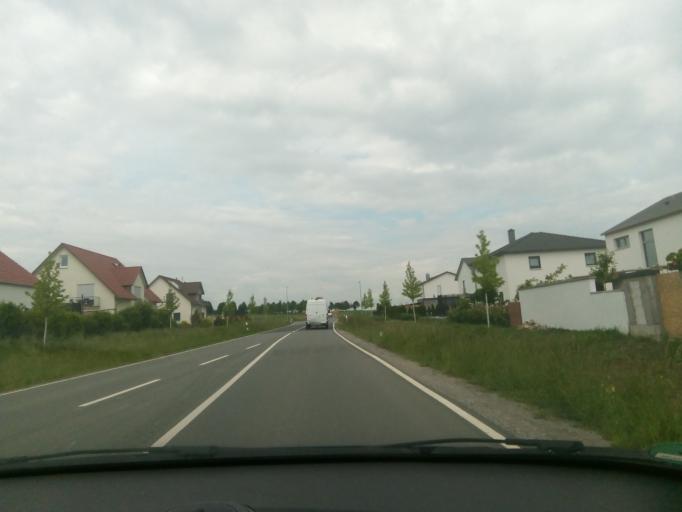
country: DE
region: Bavaria
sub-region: Regierungsbezirk Unterfranken
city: Kurnach
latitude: 49.8502
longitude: 10.0504
